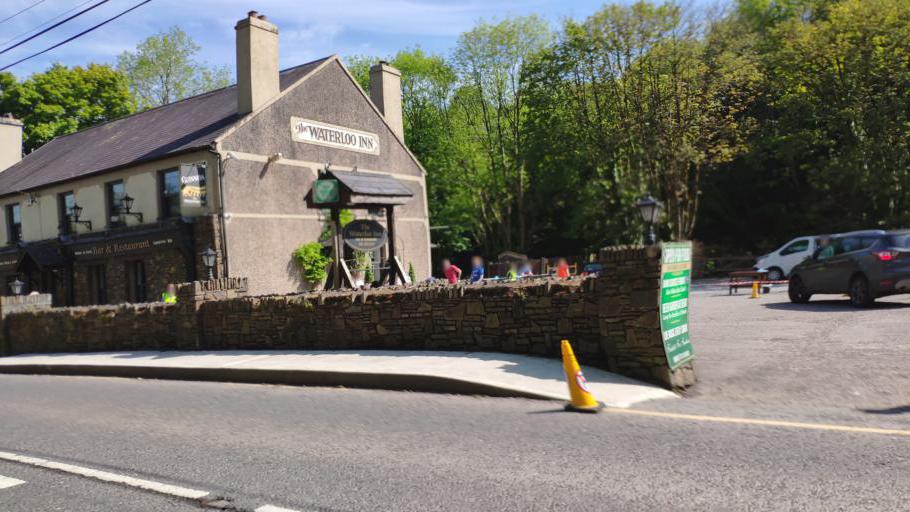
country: IE
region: Munster
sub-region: County Cork
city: Blarney
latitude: 51.9535
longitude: -8.5737
